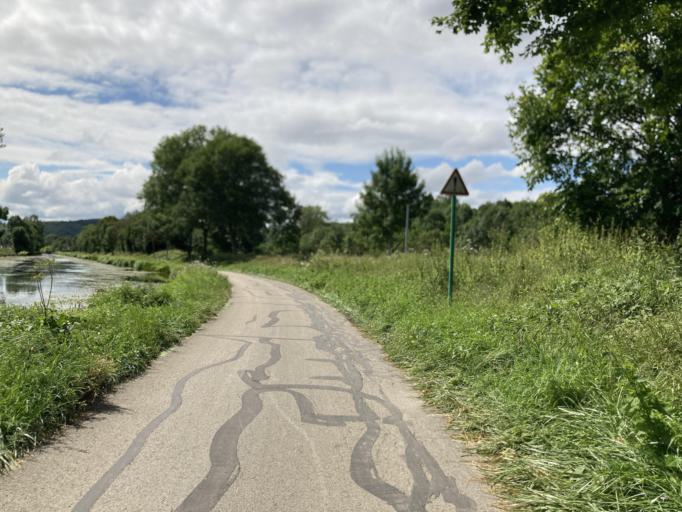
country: FR
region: Bourgogne
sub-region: Departement de la Cote-d'Or
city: Plombieres-les-Dijon
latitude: 47.3383
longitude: 4.9615
